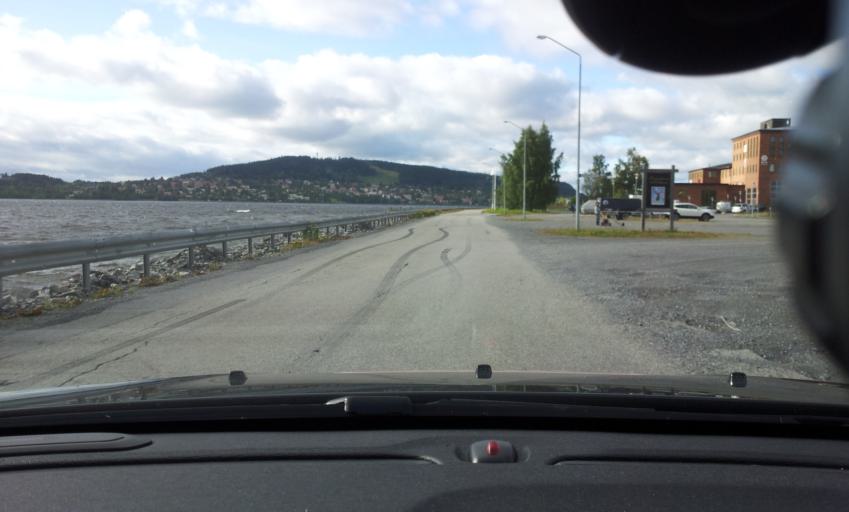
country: SE
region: Jaemtland
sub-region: OEstersunds Kommun
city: Ostersund
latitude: 63.1639
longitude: 14.6428
